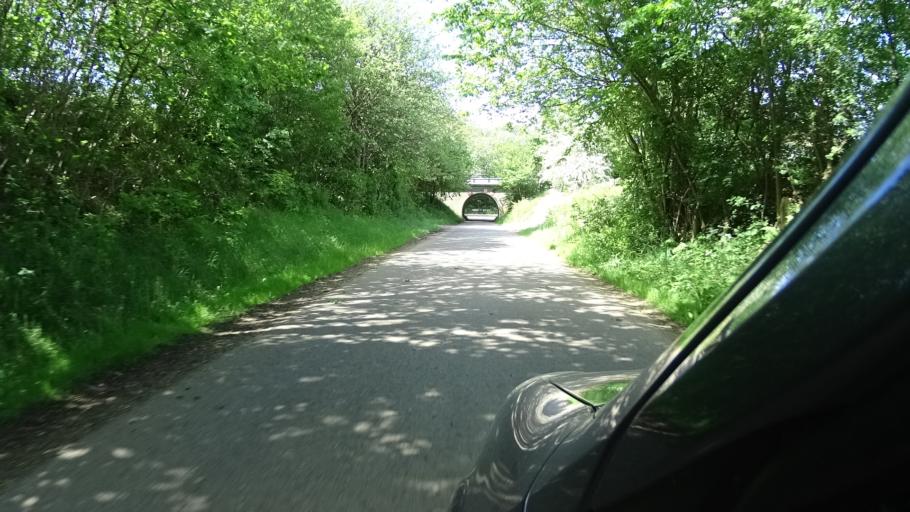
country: DK
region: South Denmark
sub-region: Vejle Kommune
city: Borkop
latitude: 55.6190
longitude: 9.6618
